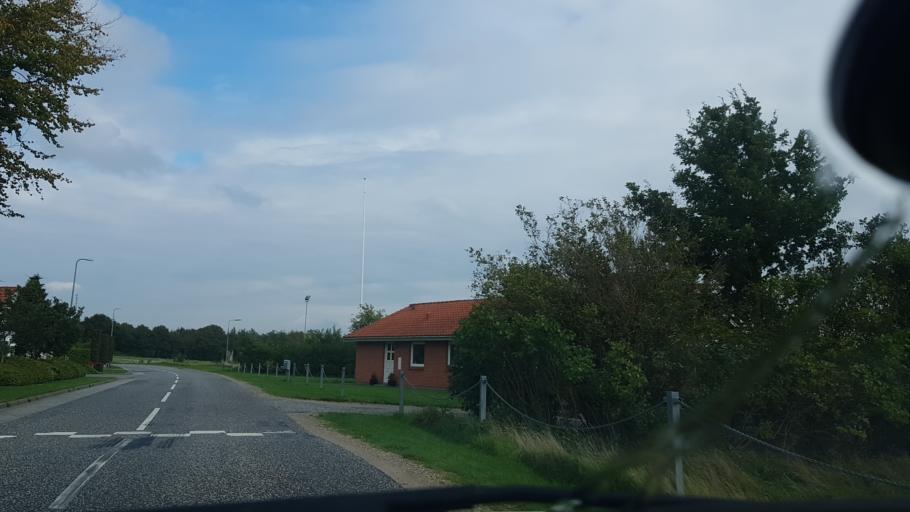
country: DK
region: South Denmark
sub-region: Billund Kommune
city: Billund
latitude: 55.6277
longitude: 9.0738
